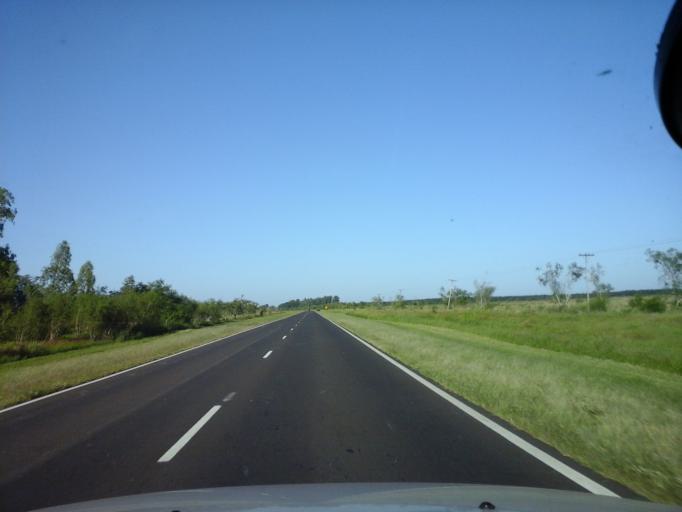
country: AR
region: Corrientes
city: Ita Ibate
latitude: -27.4448
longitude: -57.3842
